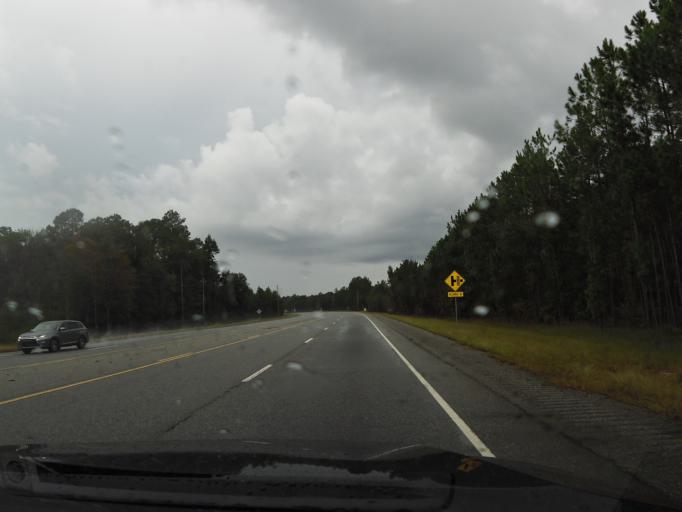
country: US
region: Georgia
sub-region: Wayne County
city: Jesup
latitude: 31.5505
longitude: -81.8127
